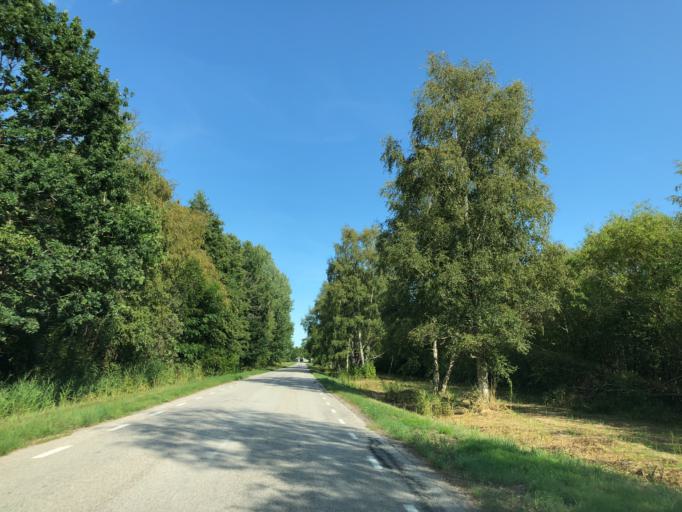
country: EE
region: Hiiumaa
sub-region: Kaerdla linn
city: Kardla
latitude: 58.8238
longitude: 22.7531
